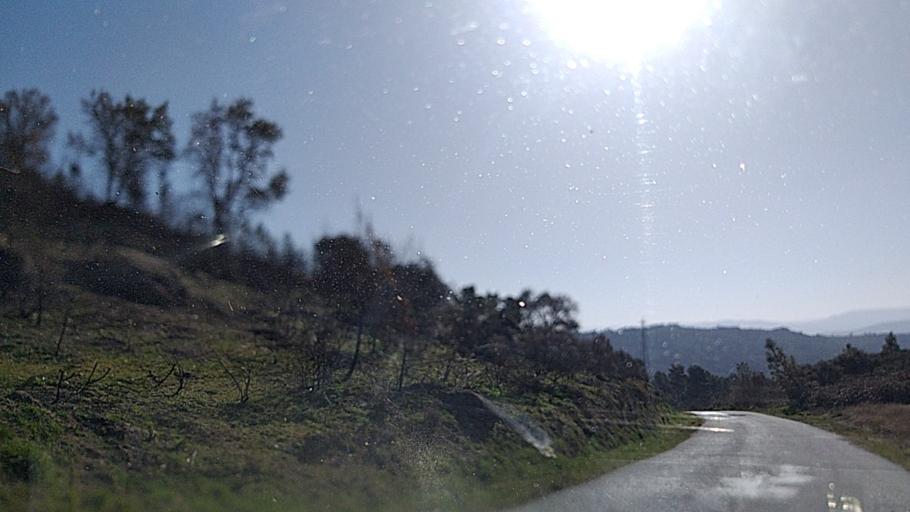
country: PT
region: Guarda
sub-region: Celorico da Beira
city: Celorico da Beira
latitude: 40.6887
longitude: -7.4182
